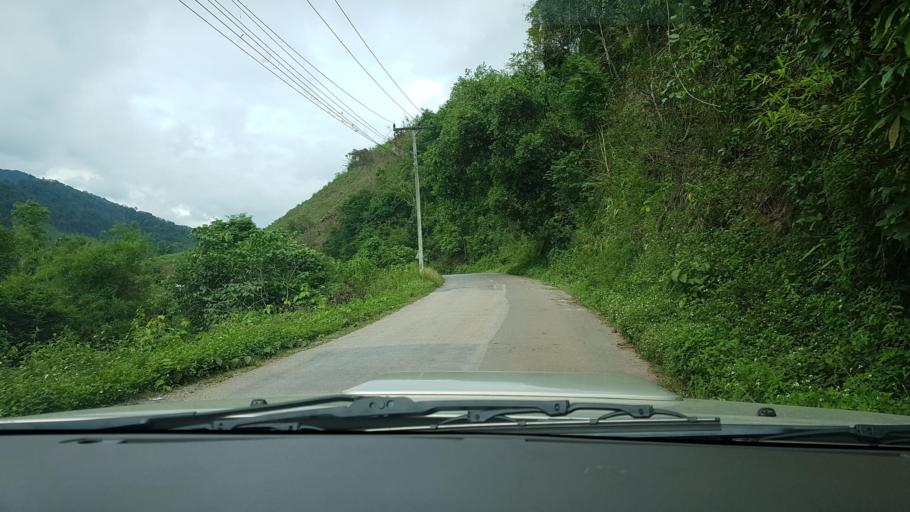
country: LA
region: Oudomxai
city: Muang Xay
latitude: 20.5612
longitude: 101.9151
